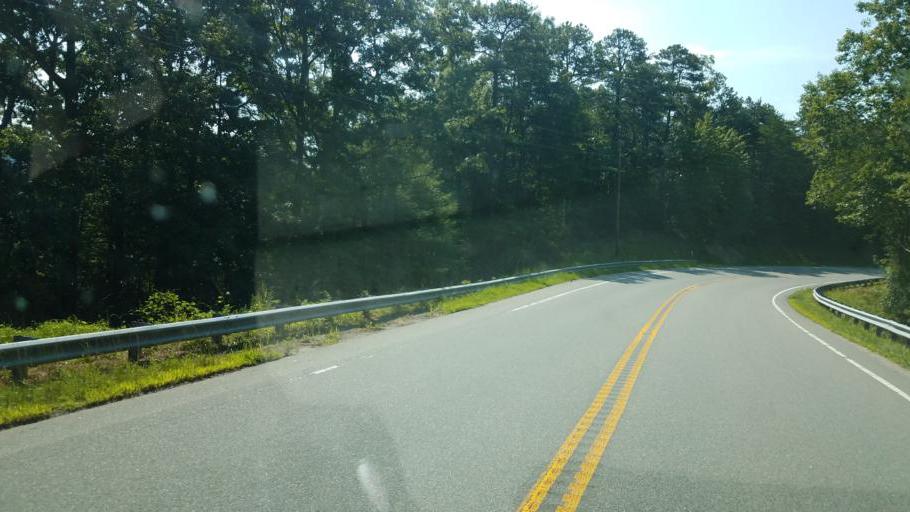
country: US
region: North Carolina
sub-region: Burke County
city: Glen Alpine
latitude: 35.9113
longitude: -81.8084
